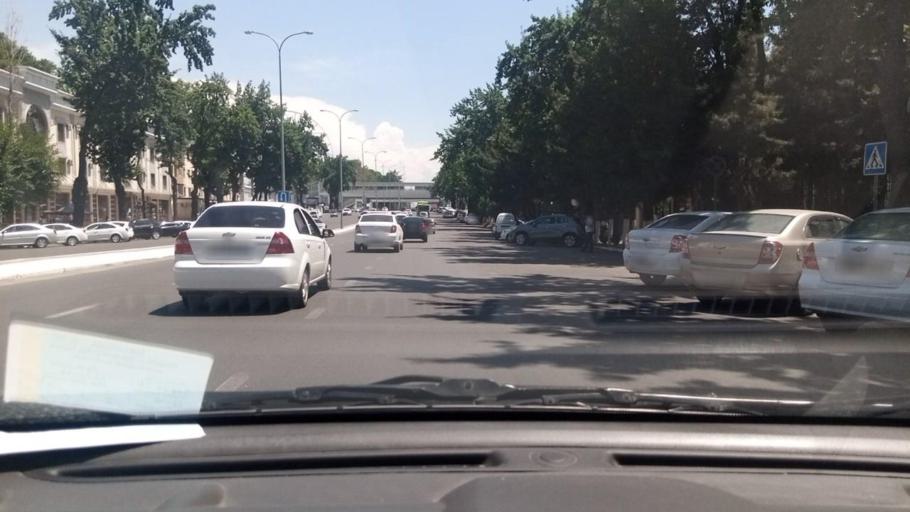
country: UZ
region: Toshkent Shahri
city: Tashkent
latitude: 41.2840
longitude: 69.2094
